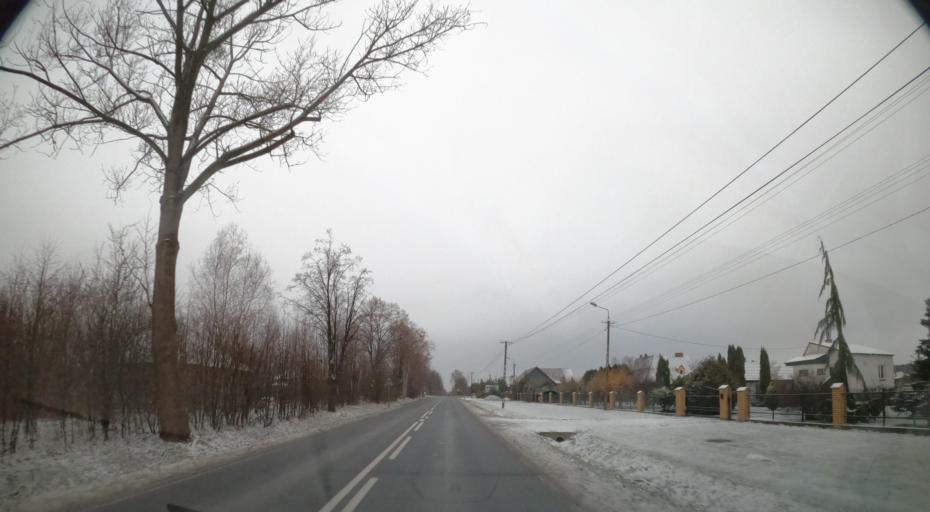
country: PL
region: Masovian Voivodeship
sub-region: Powiat plocki
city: Maszewo Duze
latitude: 52.5710
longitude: 19.6090
